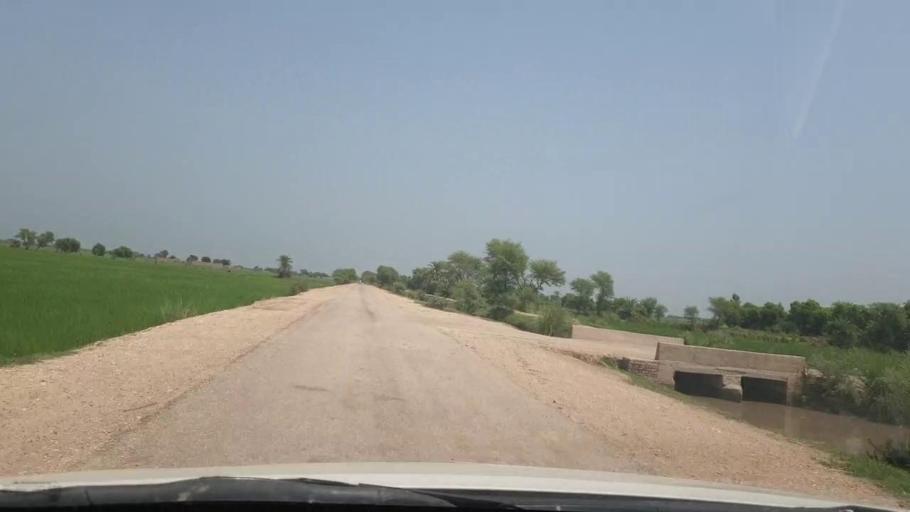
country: PK
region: Sindh
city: Rustam jo Goth
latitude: 28.0281
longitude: 68.7700
